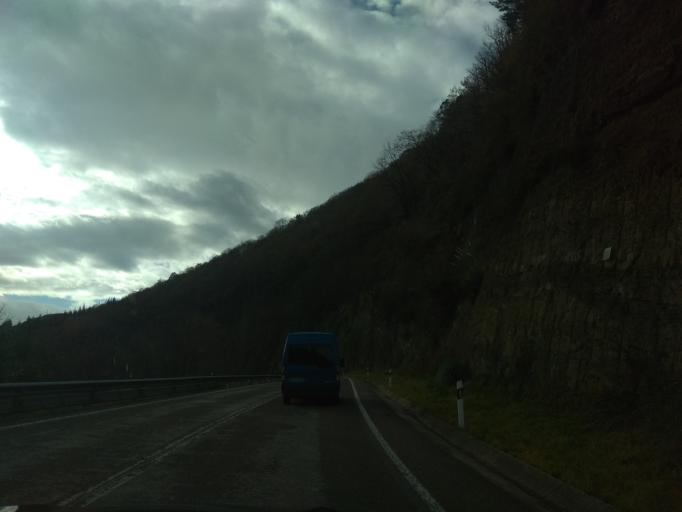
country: ES
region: Cantabria
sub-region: Provincia de Cantabria
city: San Pedro del Romeral
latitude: 43.1405
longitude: -3.8998
